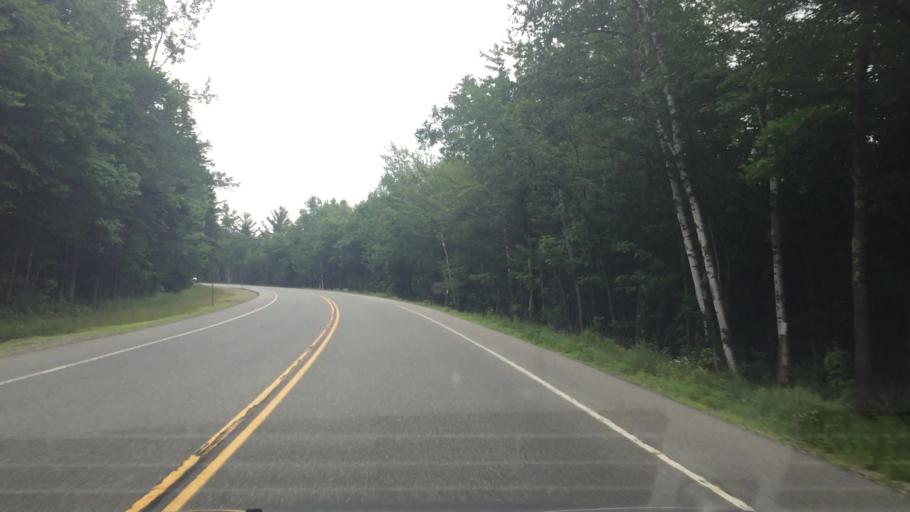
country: US
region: New Hampshire
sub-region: Grafton County
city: Deerfield
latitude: 44.2290
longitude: -71.6735
